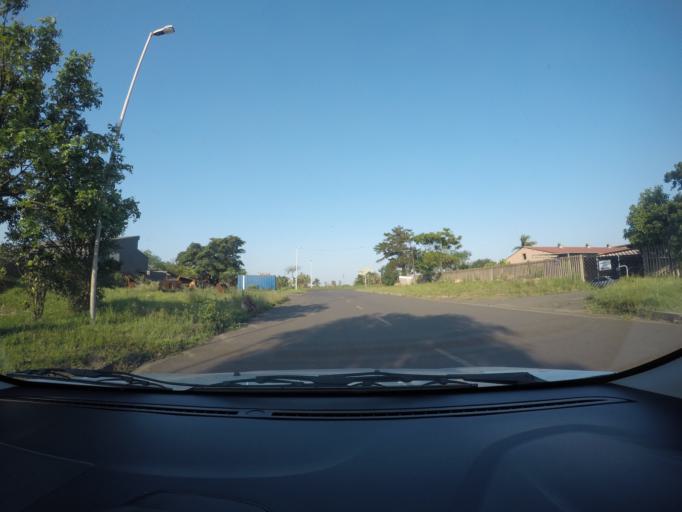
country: ZA
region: KwaZulu-Natal
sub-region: uThungulu District Municipality
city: Richards Bay
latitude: -28.7640
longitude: 32.0068
